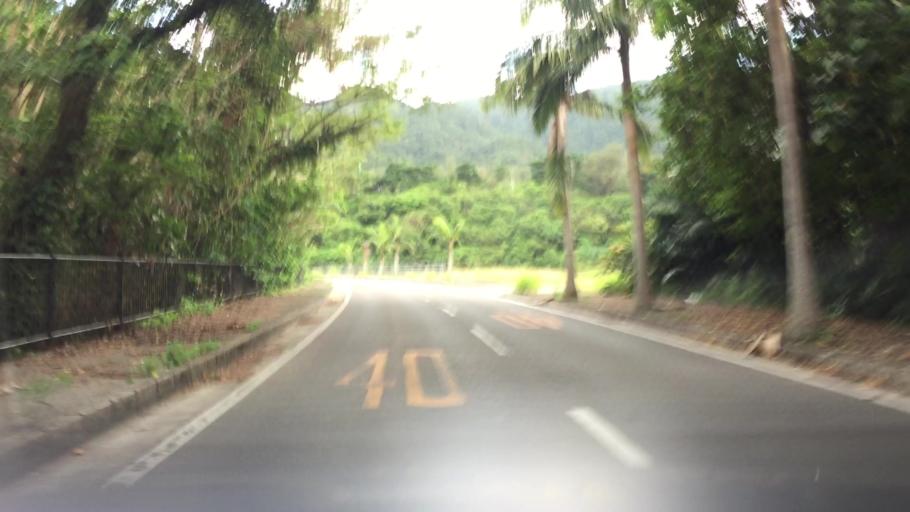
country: JP
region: Okinawa
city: Ishigaki
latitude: 24.4432
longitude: 124.1372
